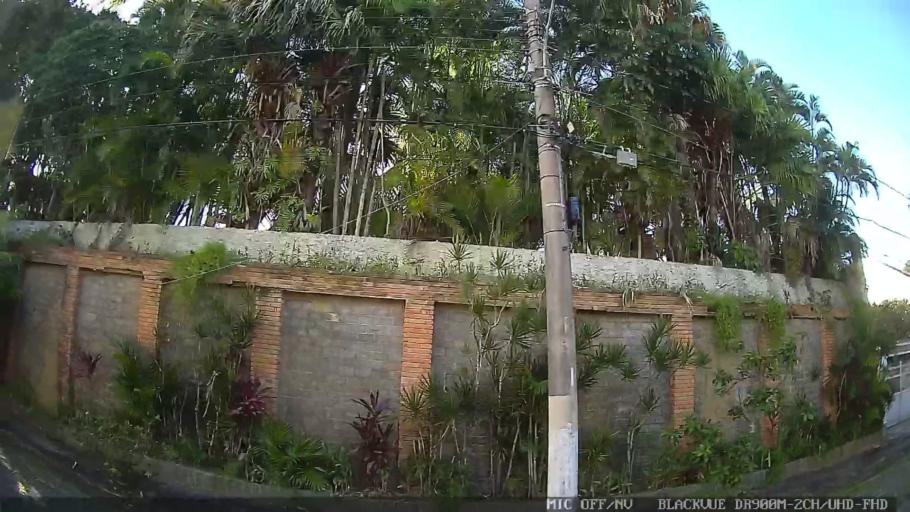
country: BR
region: Sao Paulo
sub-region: Peruibe
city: Peruibe
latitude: -24.3271
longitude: -46.9995
